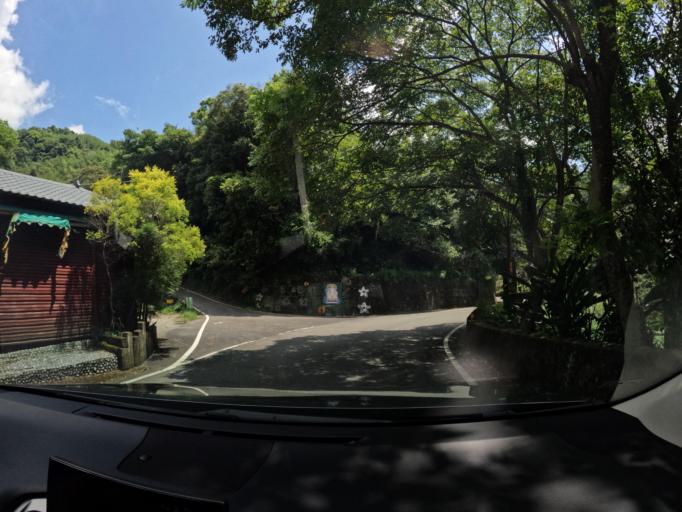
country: TW
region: Taiwan
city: Fengyuan
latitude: 24.3819
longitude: 120.8303
